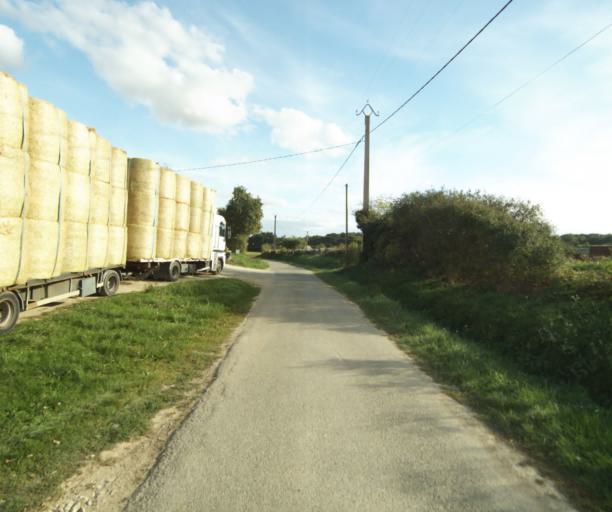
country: FR
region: Midi-Pyrenees
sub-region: Departement du Gers
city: Gondrin
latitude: 43.9119
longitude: 0.2450
